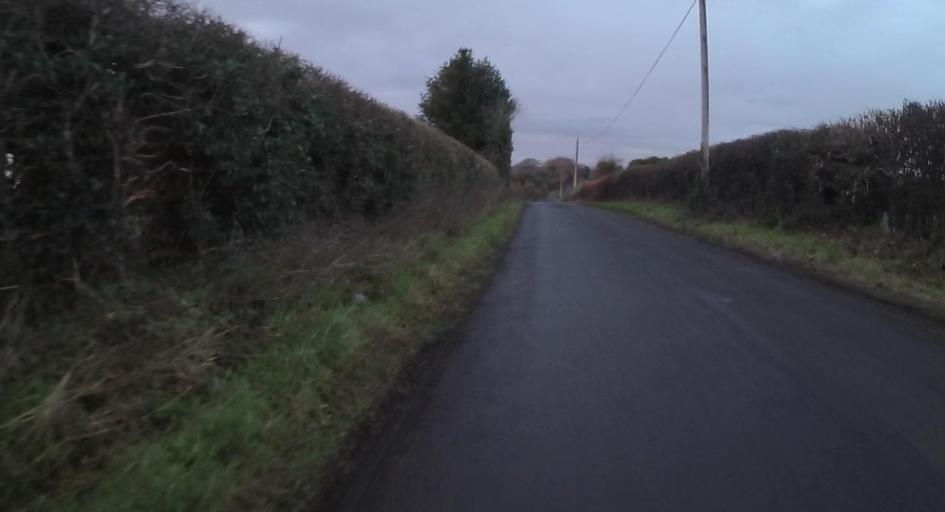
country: GB
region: England
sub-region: Hampshire
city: Four Marks
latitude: 51.0448
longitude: -1.0866
